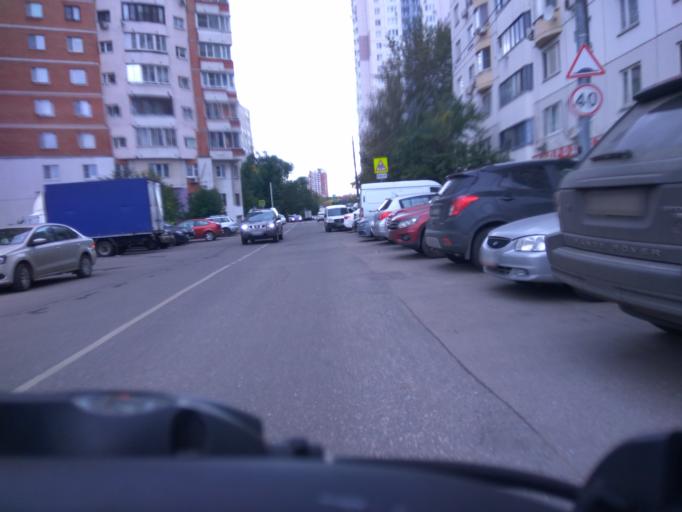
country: RU
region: Moscow
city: Slobodka
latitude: 55.8732
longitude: 37.5913
